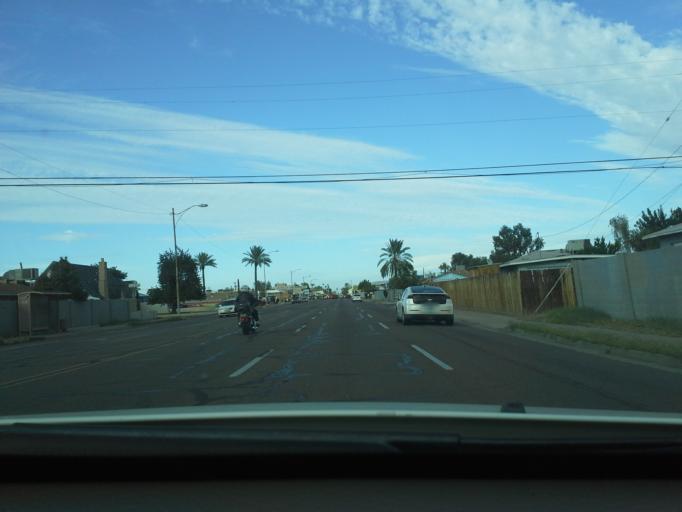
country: US
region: Arizona
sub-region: Maricopa County
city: Phoenix
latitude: 33.4906
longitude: -112.0999
